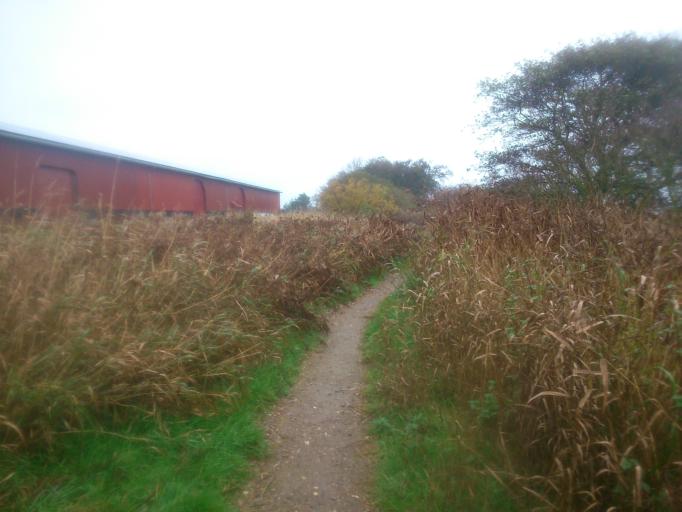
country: DK
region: South Denmark
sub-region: Varde Kommune
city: Oksbol
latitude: 55.7009
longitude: 8.2074
